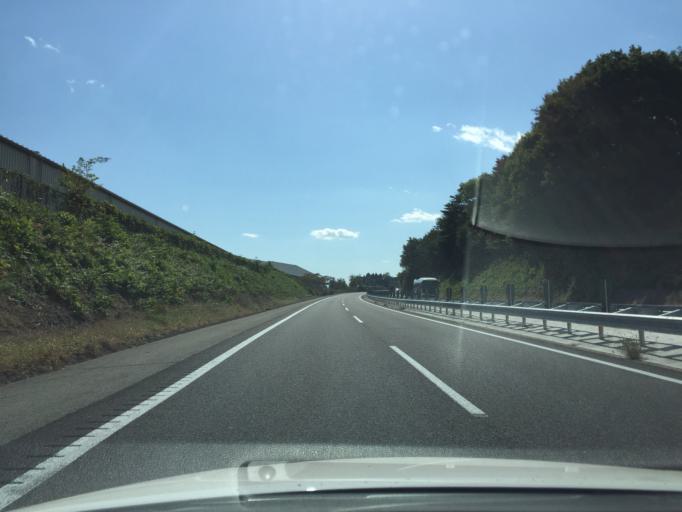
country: JP
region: Fukushima
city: Sukagawa
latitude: 37.2097
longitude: 140.3081
